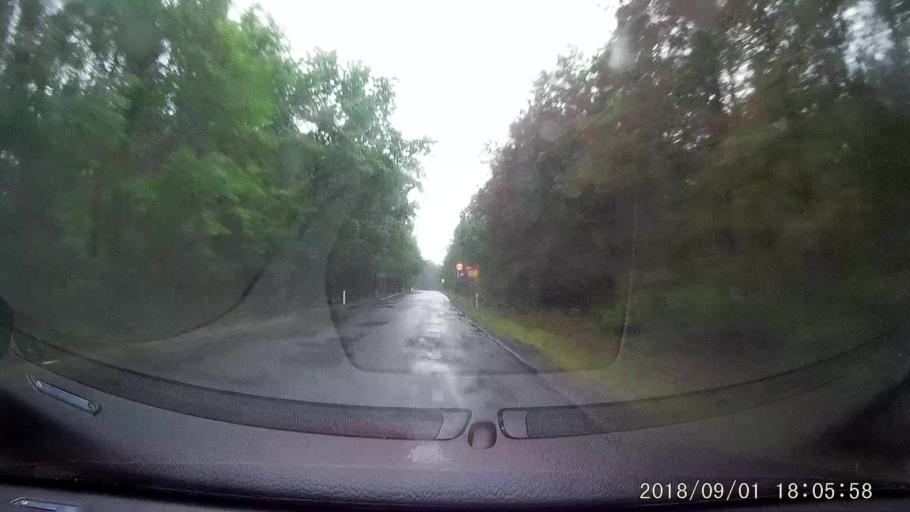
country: PL
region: Lubusz
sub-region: Powiat zaganski
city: Gozdnica
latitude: 51.3590
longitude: 15.1588
